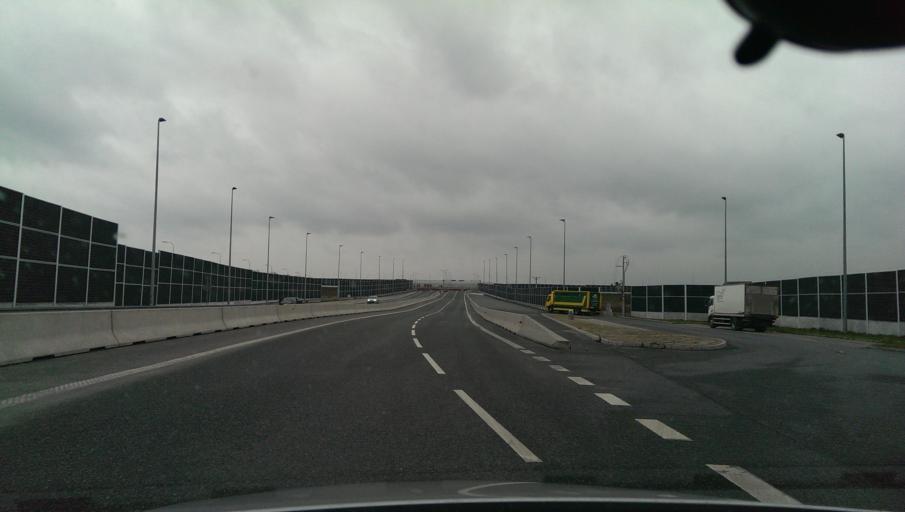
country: PL
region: Lesser Poland Voivodeship
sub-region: Powiat tarnowski
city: Wierzchoslawice
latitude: 50.0124
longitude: 20.8747
